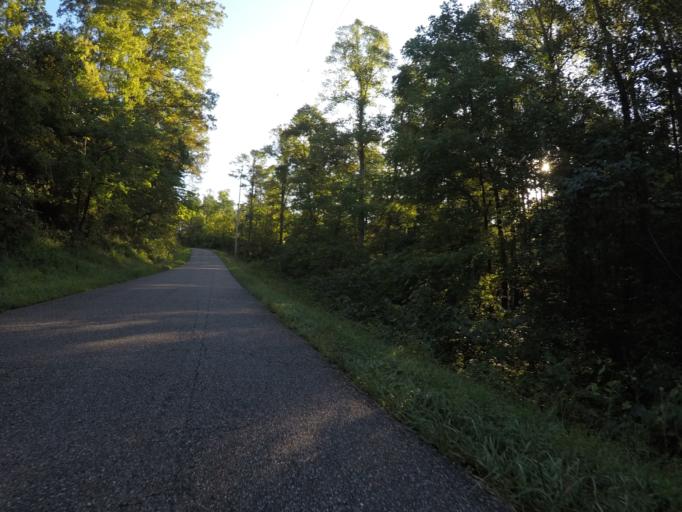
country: US
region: Ohio
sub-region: Lawrence County
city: Coal Grove
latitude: 38.6032
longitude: -82.5616
